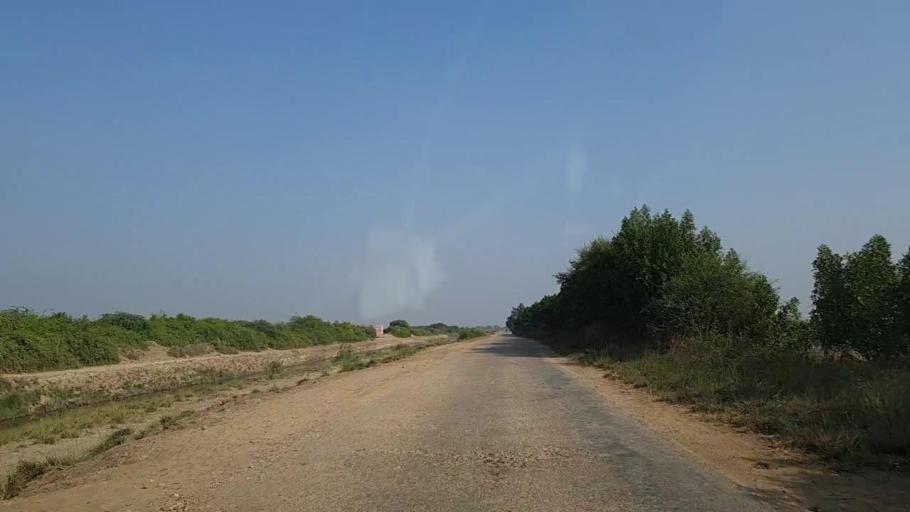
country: PK
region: Sindh
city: Mirpur Sakro
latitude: 24.6316
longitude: 67.6292
